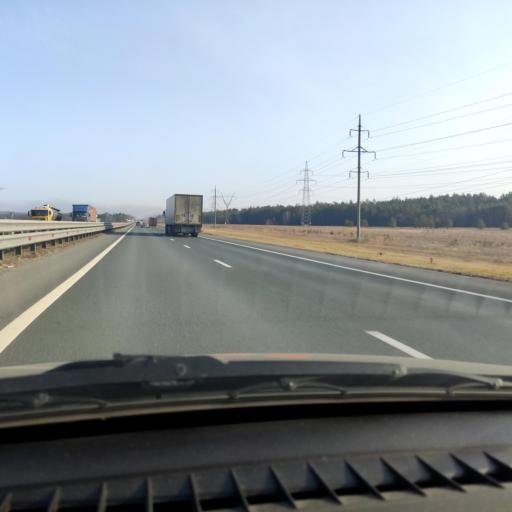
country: RU
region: Samara
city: Povolzhskiy
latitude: 53.5146
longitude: 49.6665
